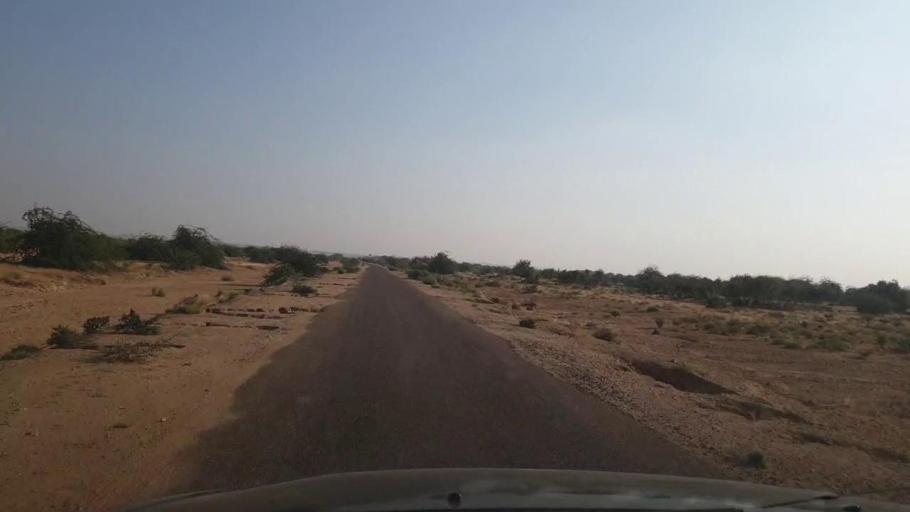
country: PK
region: Sindh
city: Jamshoro
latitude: 25.3405
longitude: 67.8402
